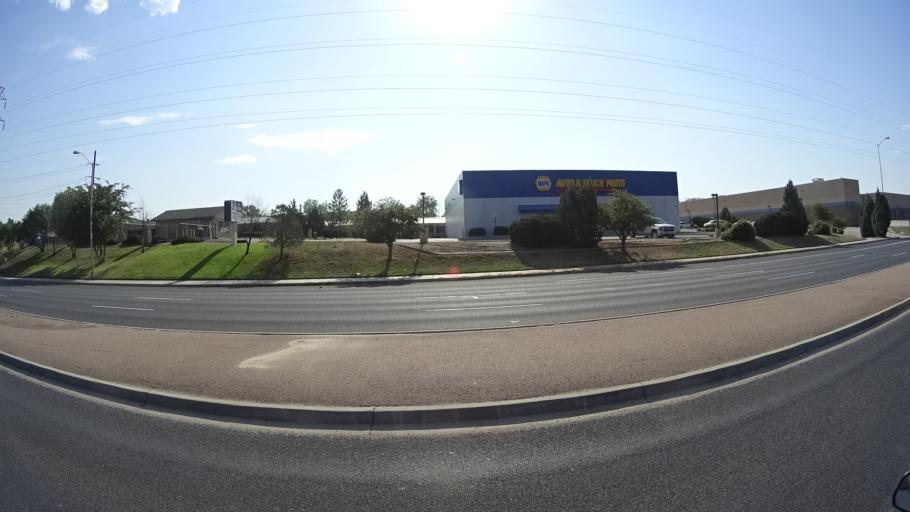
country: US
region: Colorado
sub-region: El Paso County
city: Stratmoor
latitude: 38.8210
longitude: -104.7575
